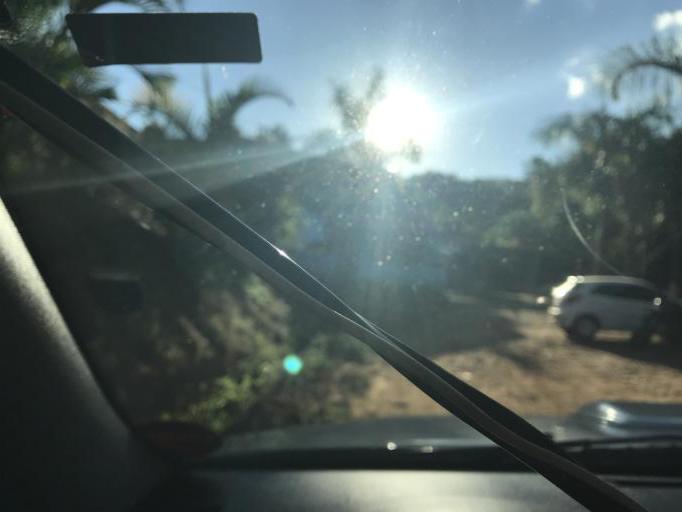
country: BR
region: Minas Gerais
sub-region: Baependi
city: Baependi
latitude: -21.9185
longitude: -44.8536
